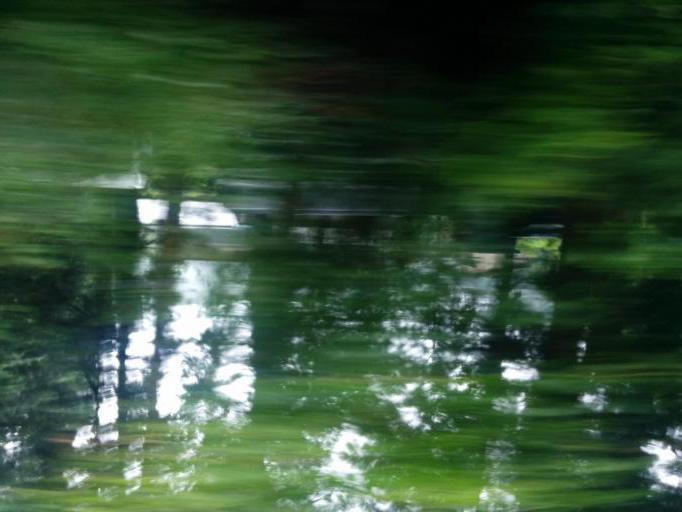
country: JP
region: Tochigi
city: Kanuma
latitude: 36.6260
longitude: 139.7311
